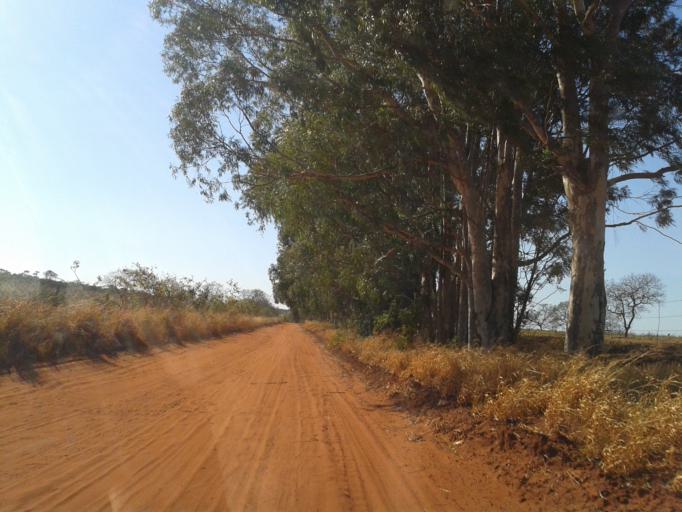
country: BR
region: Minas Gerais
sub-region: Ituiutaba
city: Ituiutaba
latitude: -18.9935
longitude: -49.3797
